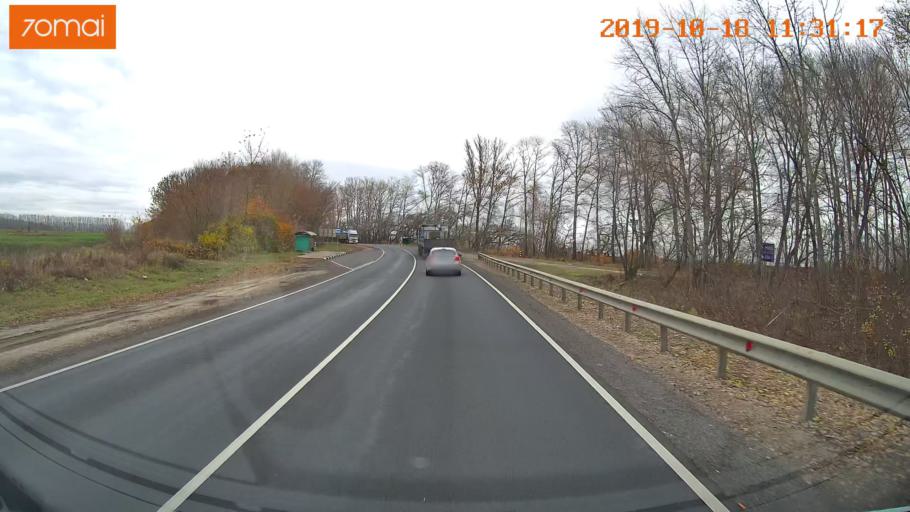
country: RU
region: Rjazan
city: Oktyabr'skiy
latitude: 54.1414
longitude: 38.6935
